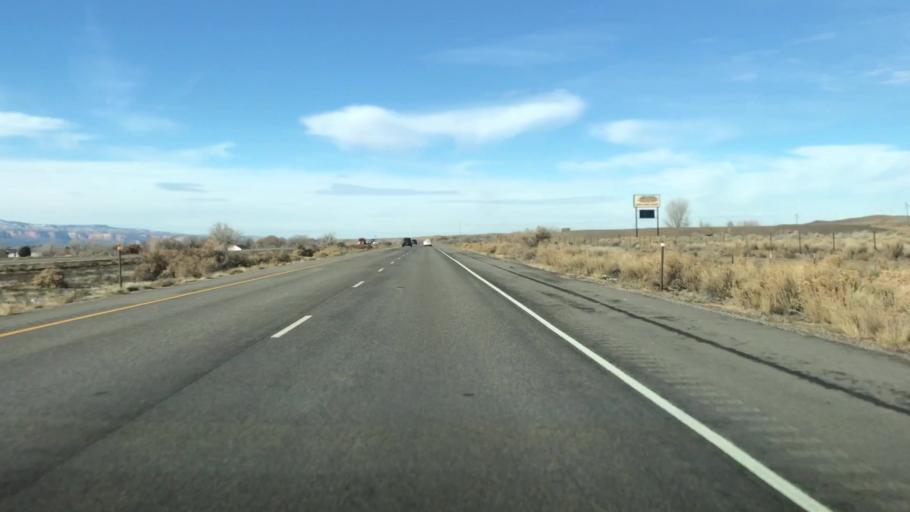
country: US
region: Colorado
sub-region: Mesa County
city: Fruitvale
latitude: 39.1062
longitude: -108.4894
